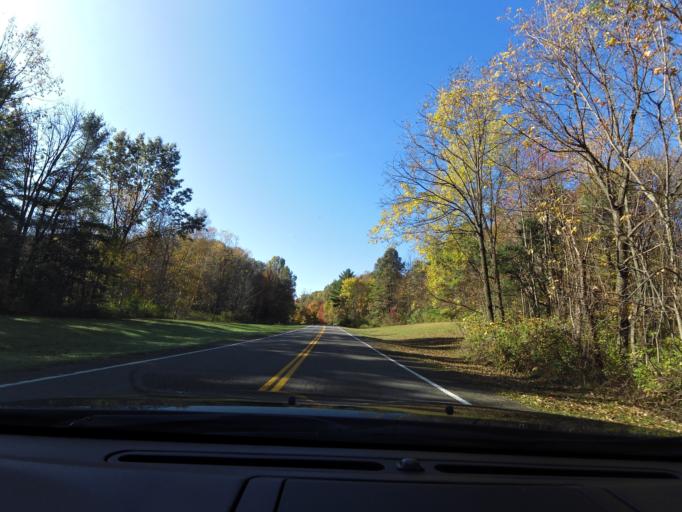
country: US
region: New York
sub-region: Wyoming County
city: Perry
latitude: 42.6921
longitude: -77.9603
